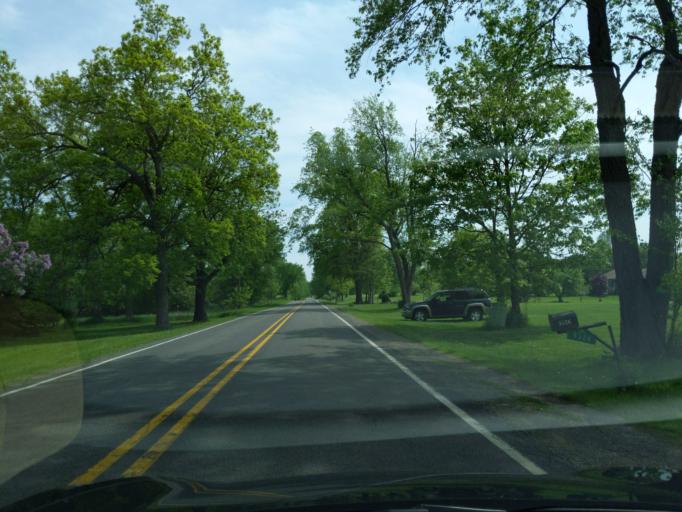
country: US
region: Michigan
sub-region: Ingham County
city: Leslie
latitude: 42.4313
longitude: -84.3560
